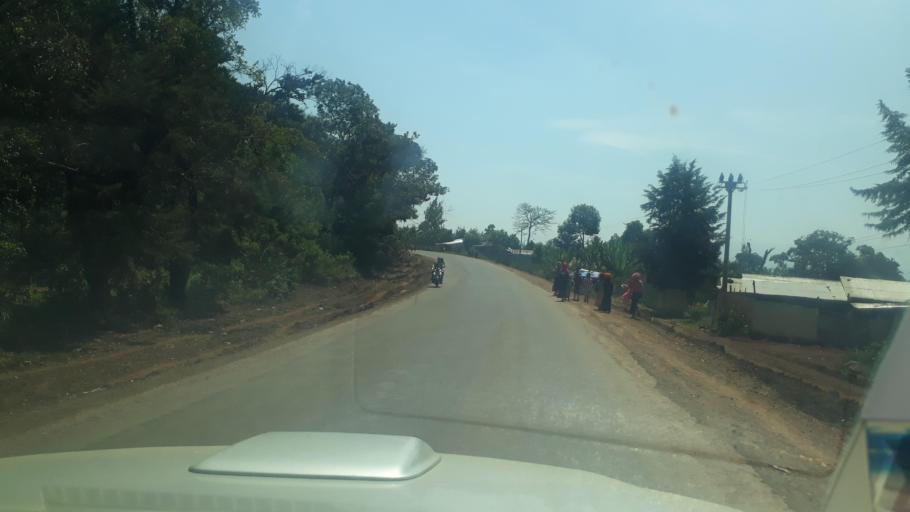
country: ET
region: Oromiya
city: Jima
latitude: 7.7035
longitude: 36.8057
